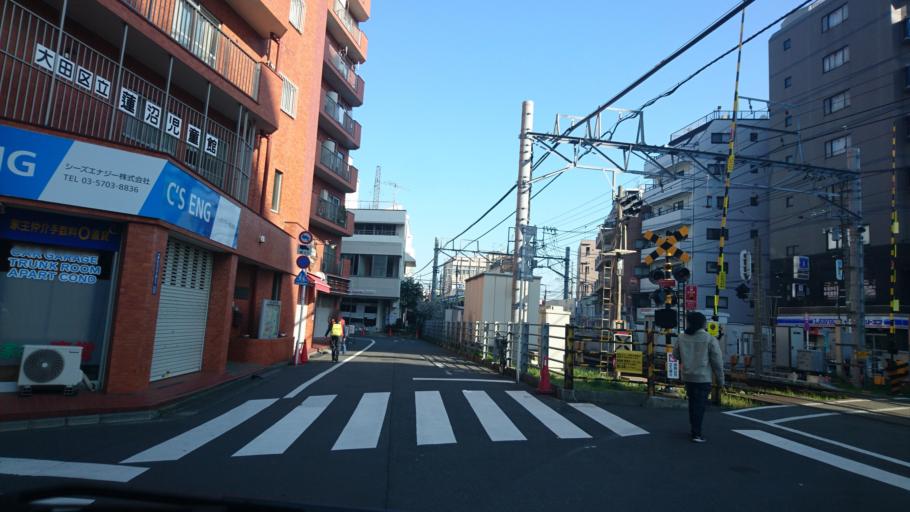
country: JP
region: Kanagawa
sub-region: Kawasaki-shi
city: Kawasaki
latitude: 35.5635
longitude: 139.7088
